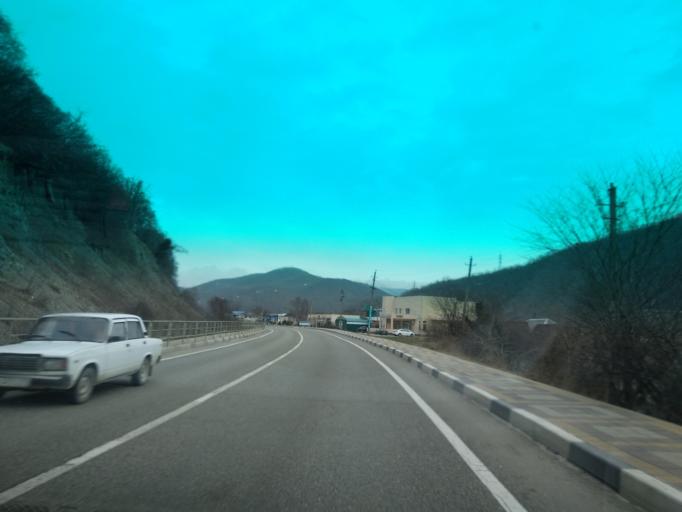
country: RU
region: Krasnodarskiy
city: Ol'ginka
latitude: 44.2061
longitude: 38.8901
